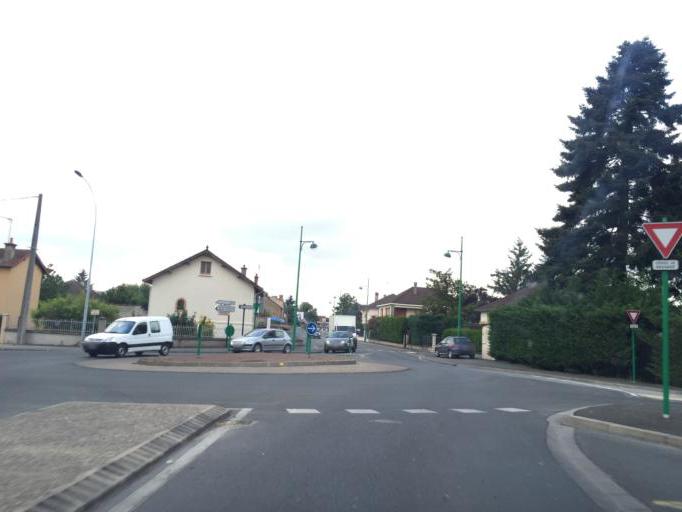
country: FR
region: Auvergne
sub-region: Departement de l'Allier
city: Yzeure
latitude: 46.5609
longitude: 3.3557
